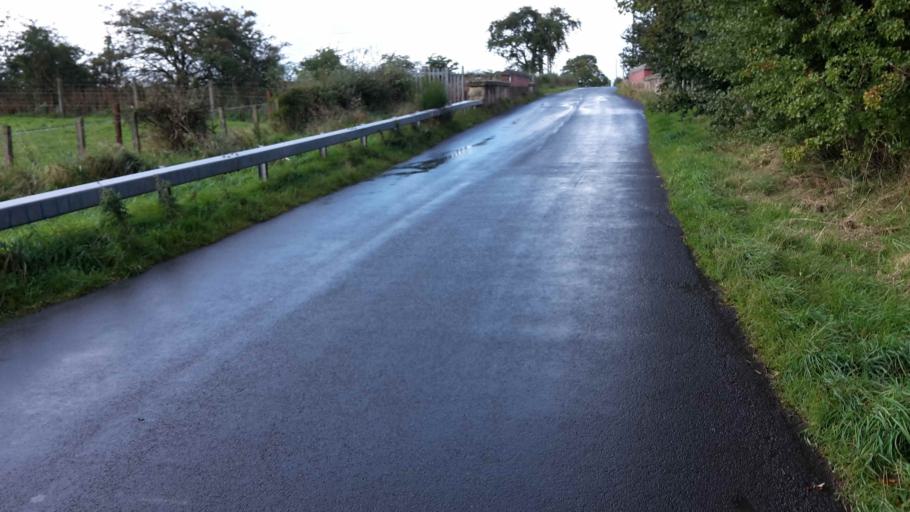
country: GB
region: Scotland
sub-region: South Lanarkshire
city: Carluke
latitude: 55.7253
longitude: -3.8411
